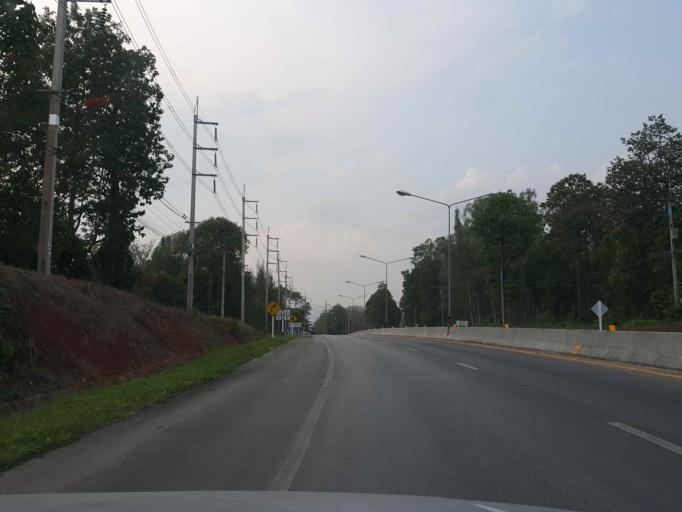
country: TH
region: Chiang Mai
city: Mae Taeng
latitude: 19.1436
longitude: 98.9475
